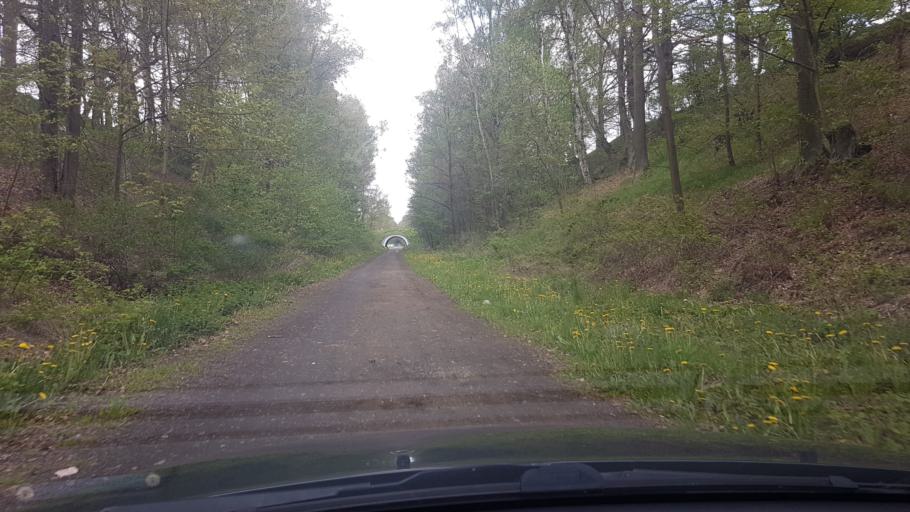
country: CZ
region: Karlovarsky
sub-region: Okres Cheb
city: Cheb
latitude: 50.0527
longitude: 12.3877
